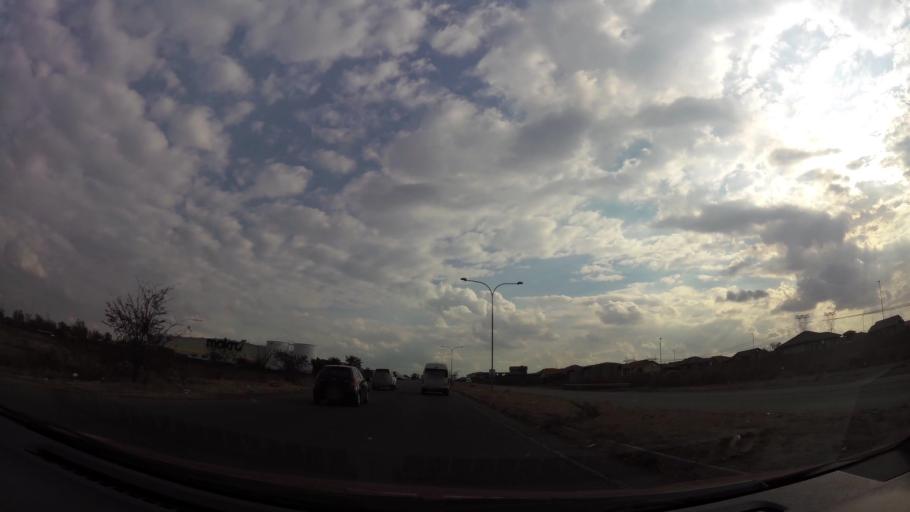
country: ZA
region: Gauteng
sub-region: Sedibeng District Municipality
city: Vanderbijlpark
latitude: -26.6976
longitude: 27.8836
